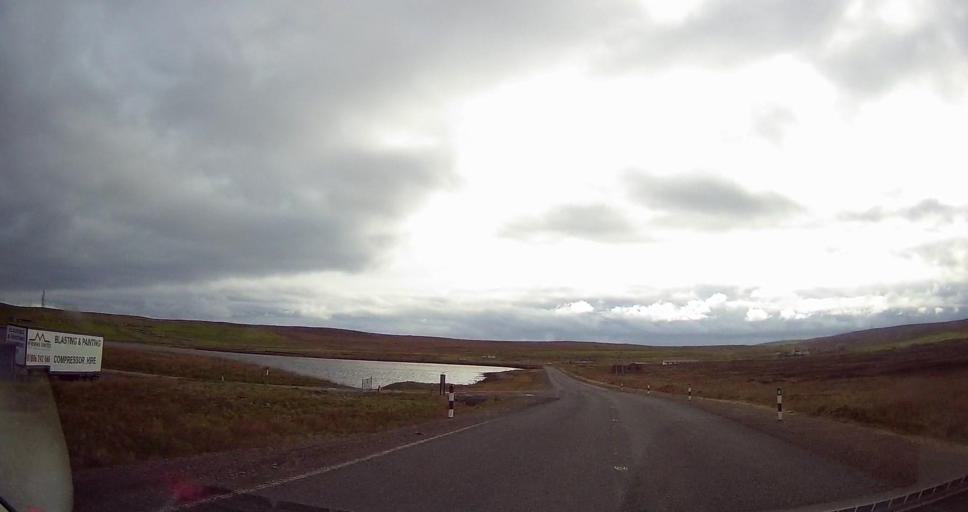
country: GB
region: Scotland
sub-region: Shetland Islands
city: Lerwick
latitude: 60.4408
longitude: -1.2702
